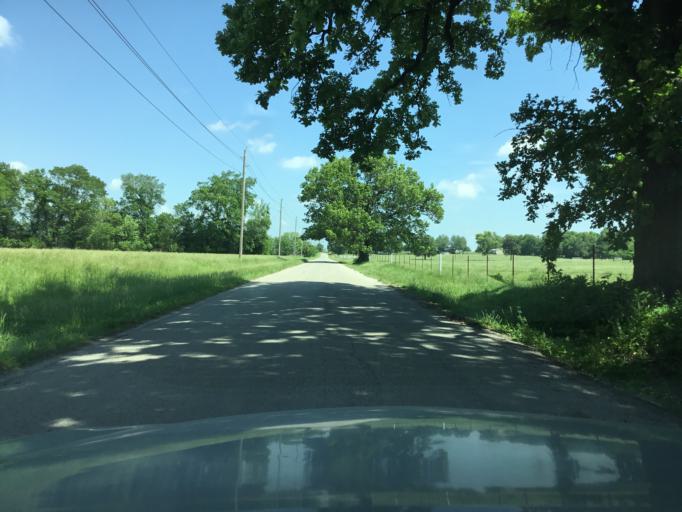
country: US
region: Kansas
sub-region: Labette County
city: Parsons
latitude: 37.3503
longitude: -95.2496
